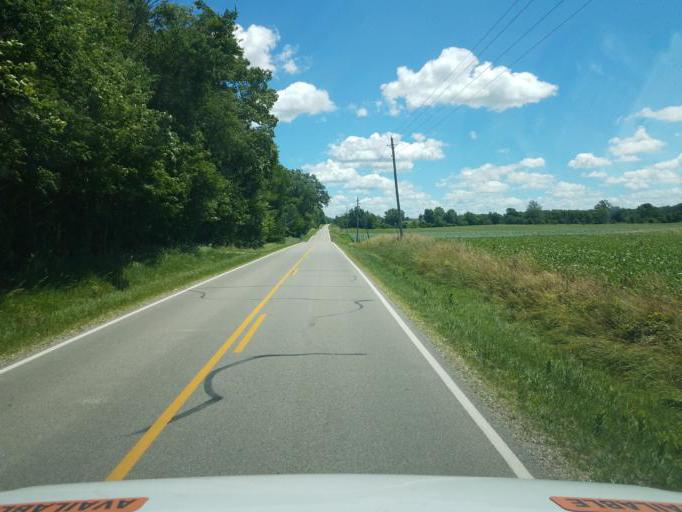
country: US
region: Ohio
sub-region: Crawford County
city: Galion
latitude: 40.7343
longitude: -82.8470
